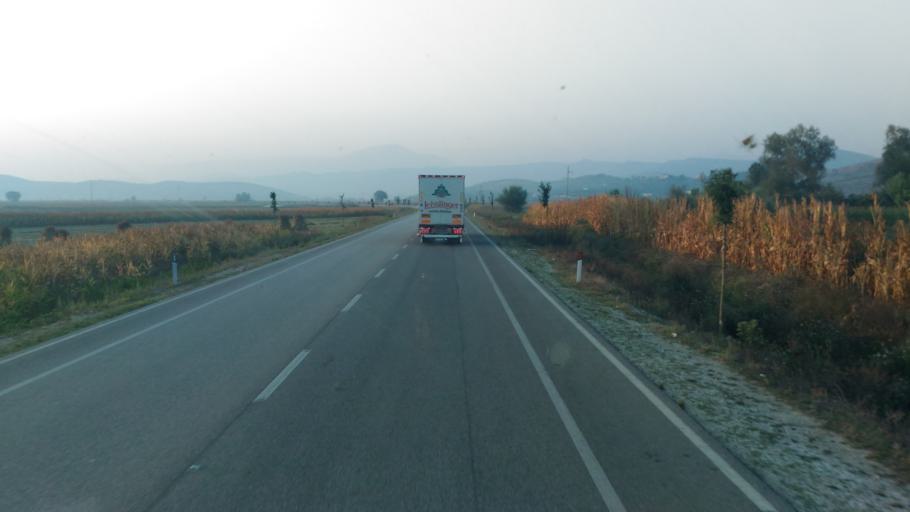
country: AL
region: Fier
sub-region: Rrethi i Fierit
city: Cakran
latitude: 40.5770
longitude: 19.6216
